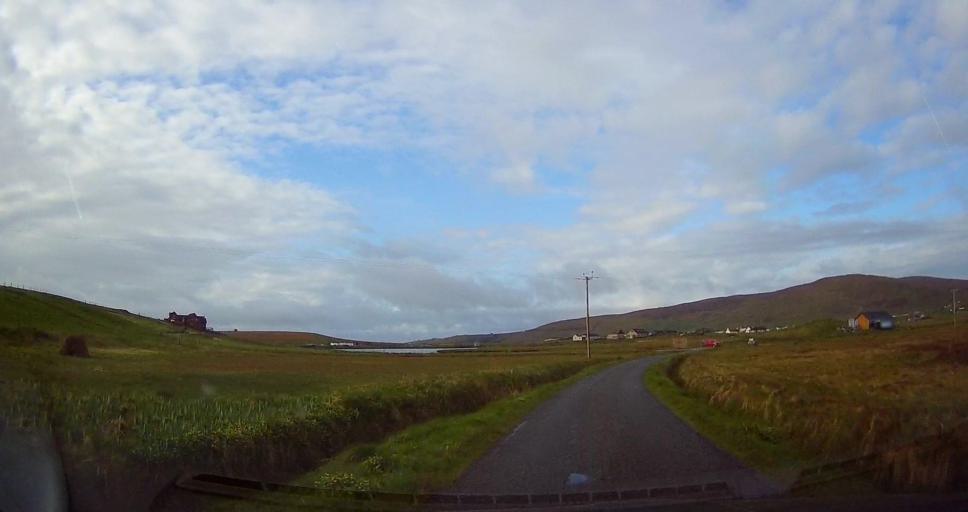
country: GB
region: Scotland
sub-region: Shetland Islands
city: Sandwick
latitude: 60.0477
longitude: -1.2075
